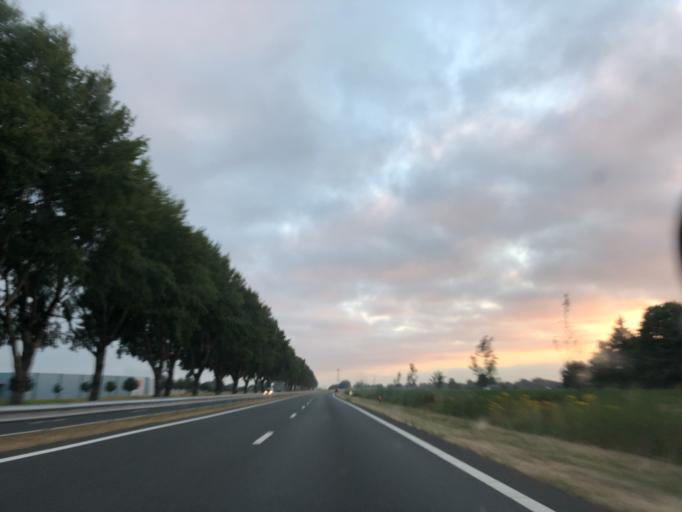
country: NL
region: Groningen
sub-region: Gemeente Veendam
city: Veendam
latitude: 53.1259
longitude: 6.8996
